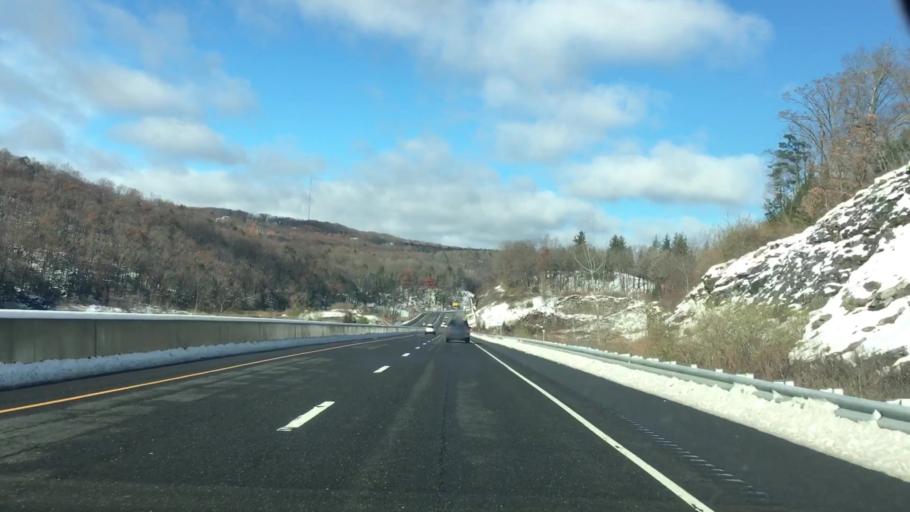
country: US
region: Connecticut
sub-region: Fairfield County
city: Danbury
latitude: 41.4792
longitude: -73.4132
